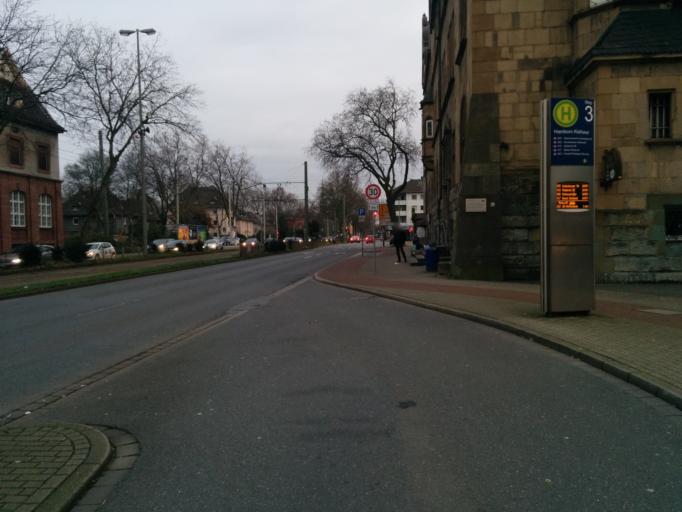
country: DE
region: North Rhine-Westphalia
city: Meiderich
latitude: 51.4939
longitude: 6.7731
